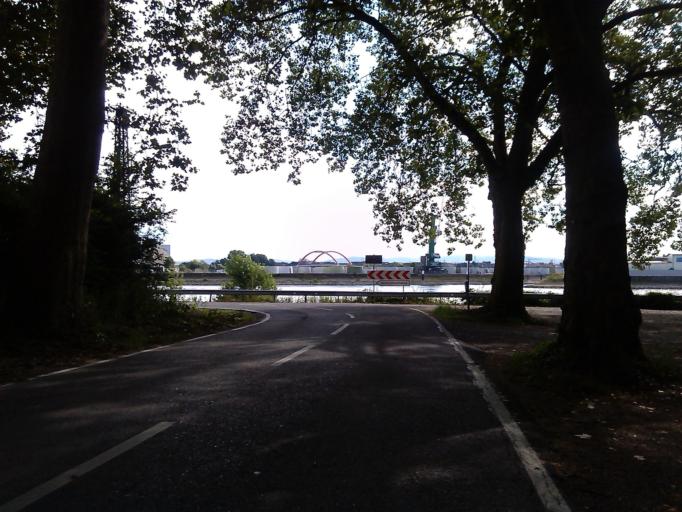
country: DE
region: Rheinland-Pfalz
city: Altrip
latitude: 49.4338
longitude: 8.5057
